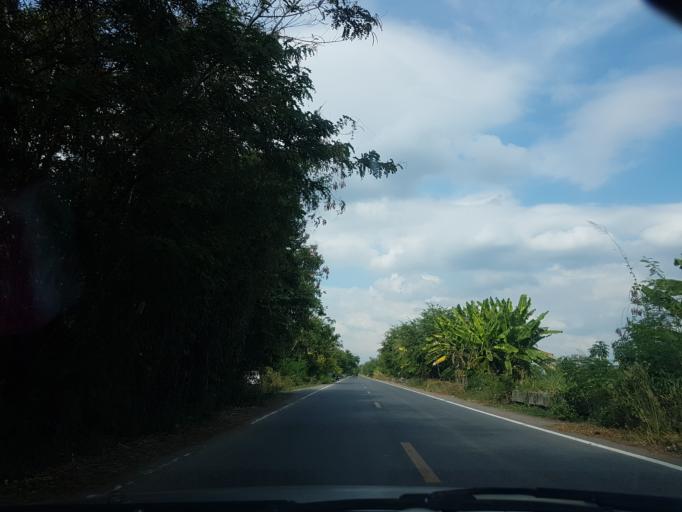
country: TH
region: Pathum Thani
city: Nong Suea
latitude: 14.1450
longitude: 100.8914
